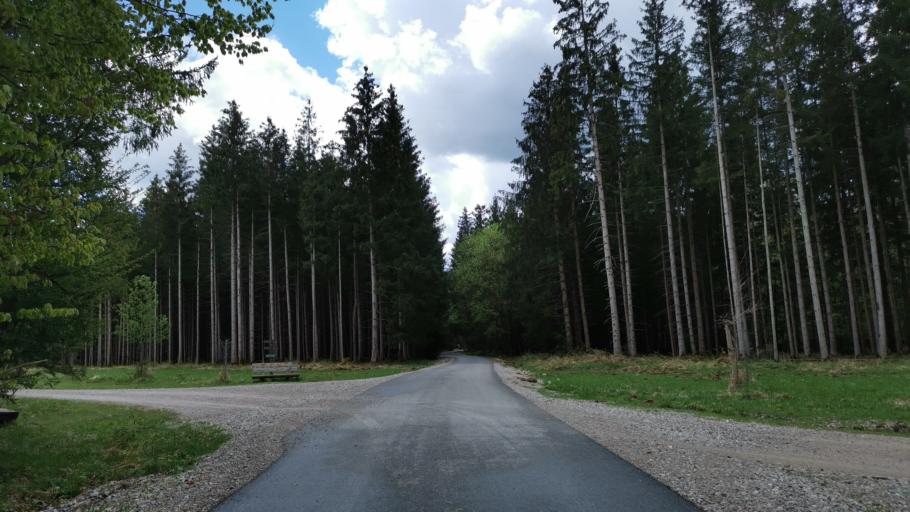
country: DE
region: Bavaria
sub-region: Upper Bavaria
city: Pullach im Isartal
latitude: 48.0674
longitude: 11.4890
